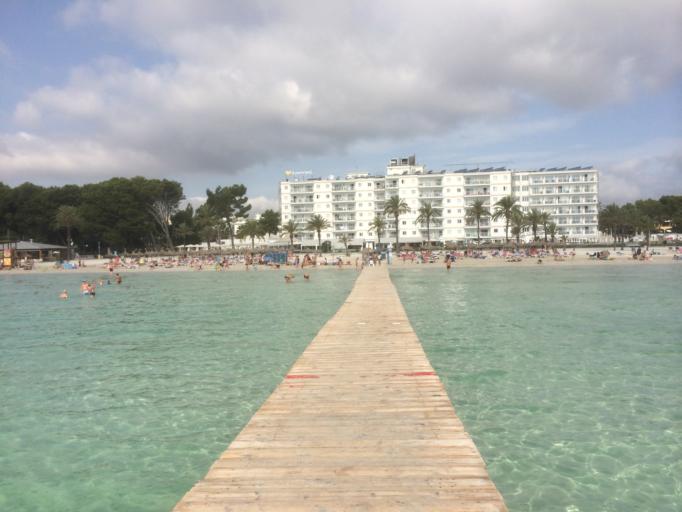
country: ES
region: Balearic Islands
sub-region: Illes Balears
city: Port d'Alcudia
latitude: 39.8360
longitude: 3.1245
